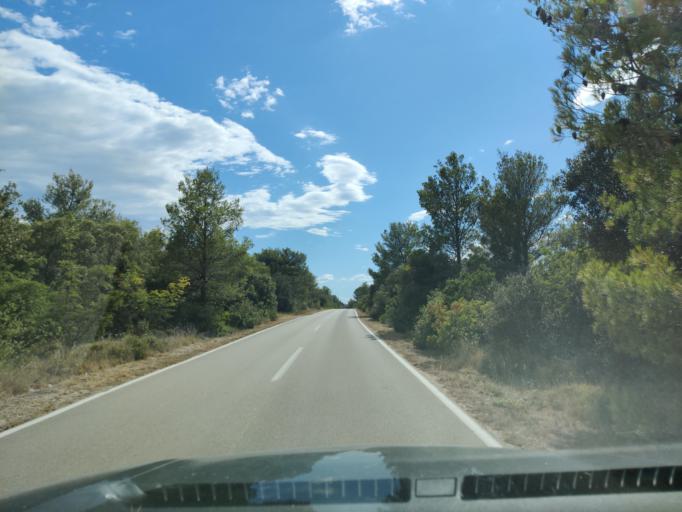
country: HR
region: Sibensko-Kniniska
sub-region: Grad Sibenik
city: Sibenik
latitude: 43.7321
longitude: 15.8537
